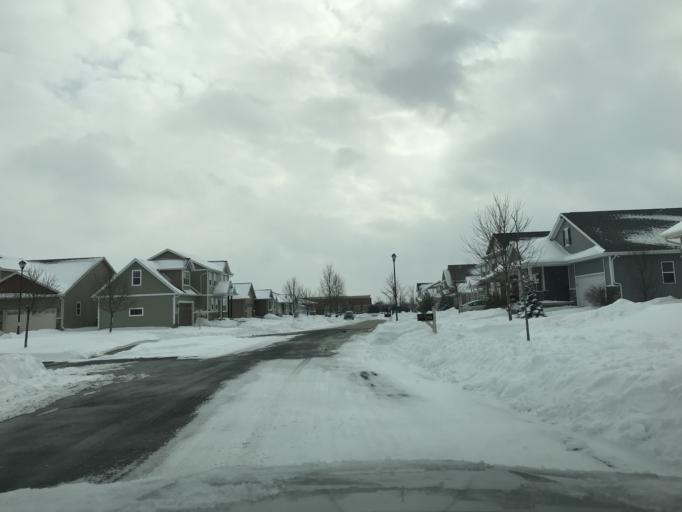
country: US
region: Wisconsin
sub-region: Dane County
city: Sun Prairie
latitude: 43.1737
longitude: -89.2689
